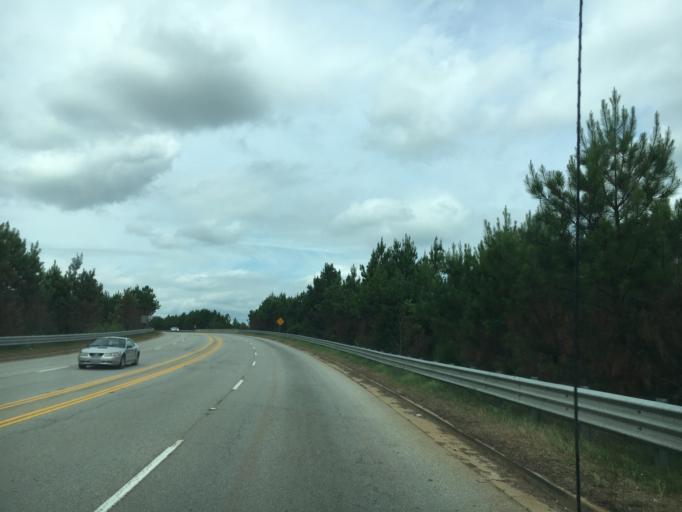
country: US
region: South Carolina
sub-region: Spartanburg County
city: Roebuck
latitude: 34.8354
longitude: -81.9852
